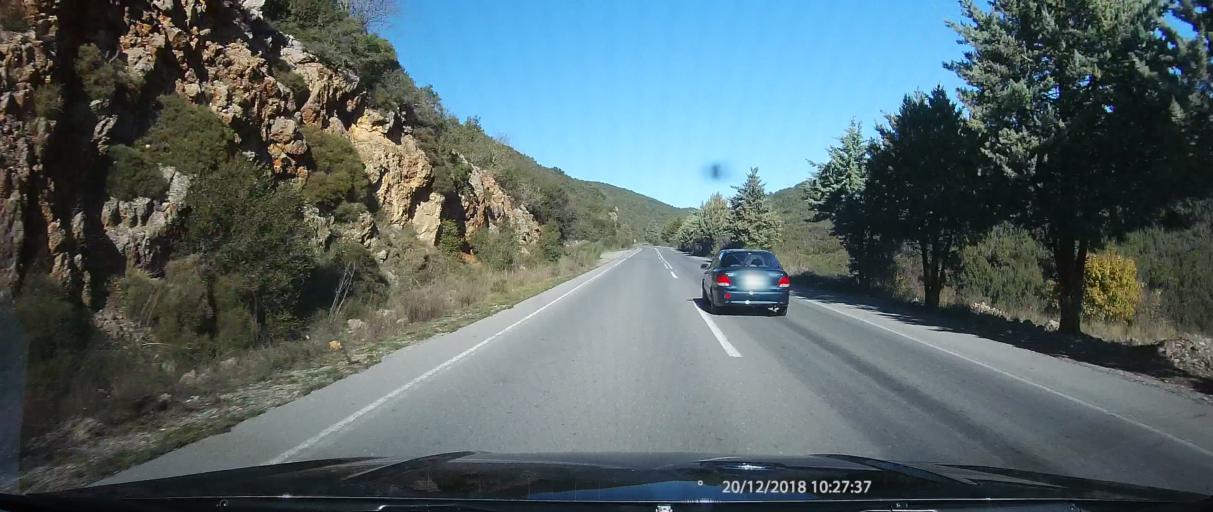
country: GR
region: Peloponnese
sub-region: Nomos Lakonias
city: Kariai
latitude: 37.2479
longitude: 22.4391
